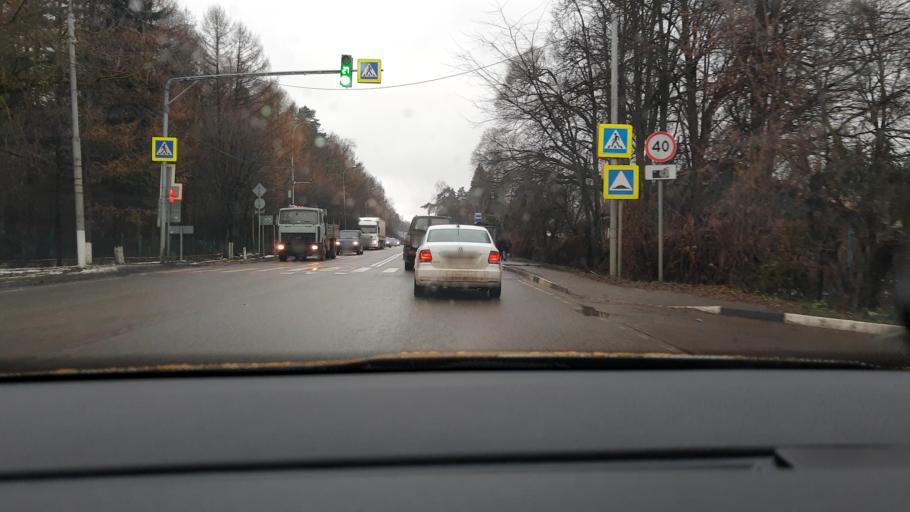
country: RU
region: Moskovskaya
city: Ivanteyevka
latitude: 55.9800
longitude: 37.8953
